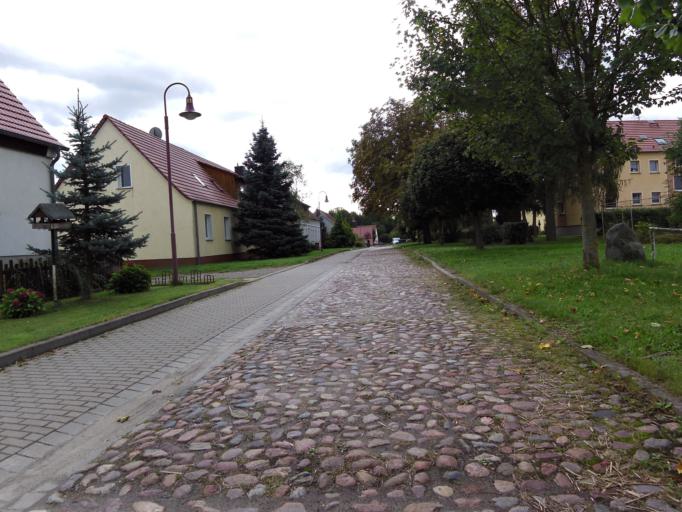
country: DE
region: Saxony-Anhalt
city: Arneburg
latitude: 52.6328
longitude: 12.0032
